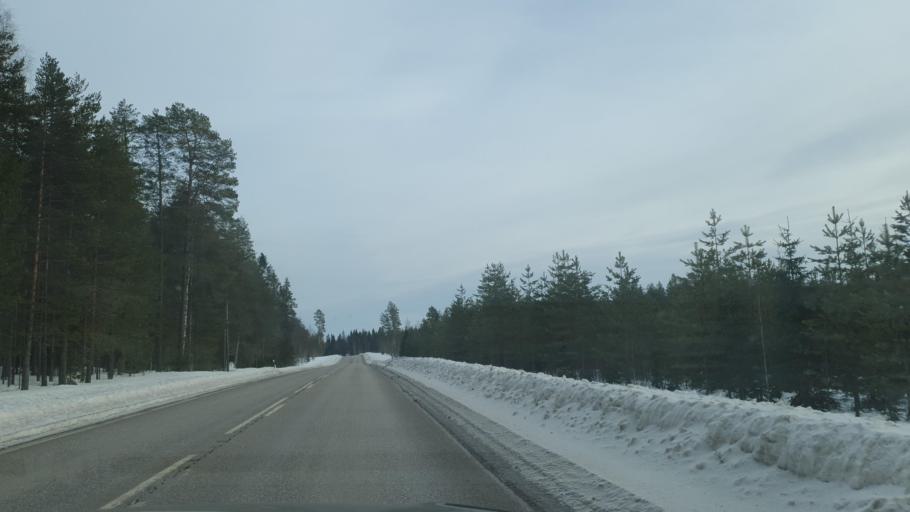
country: FI
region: Kainuu
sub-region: Kajaani
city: Vuolijoki
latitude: 64.4862
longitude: 27.3333
